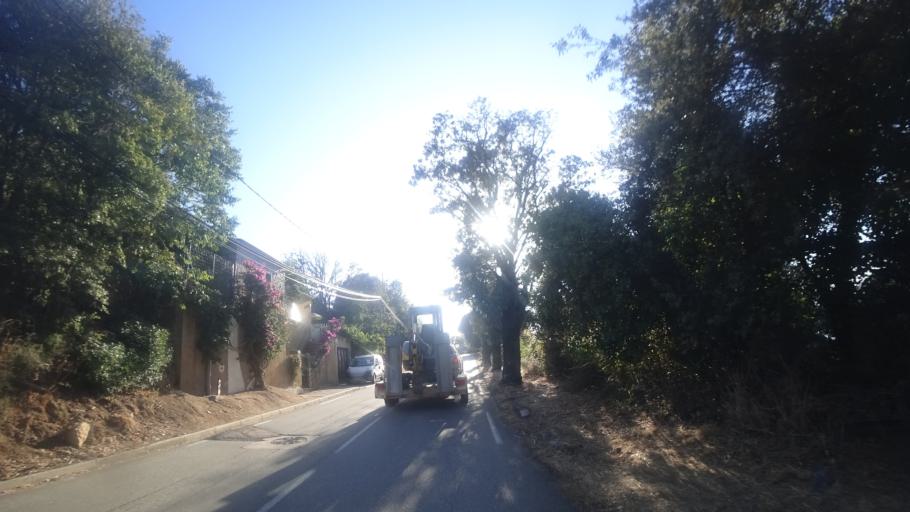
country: FR
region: Corsica
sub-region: Departement de la Corse-du-Sud
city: Cargese
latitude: 42.1385
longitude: 8.5993
